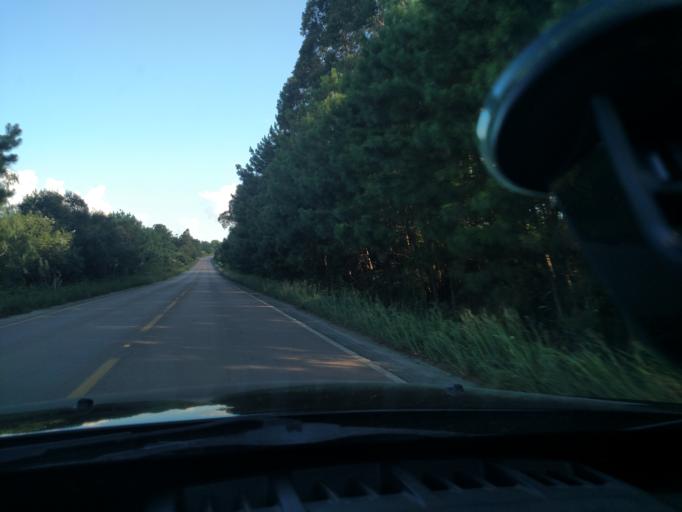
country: BR
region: Santa Catarina
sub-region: Otacilio Costa
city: Otacilio Costa
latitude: -27.4125
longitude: -50.1258
